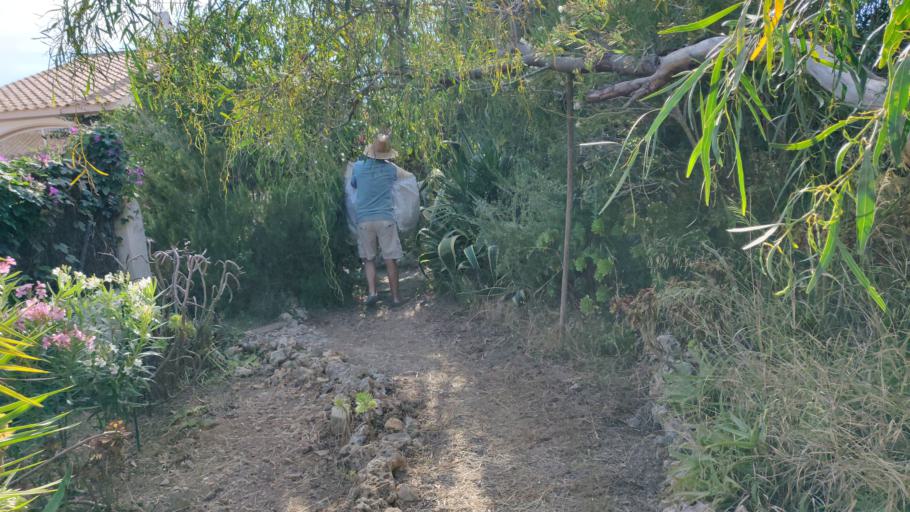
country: ES
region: Balearic Islands
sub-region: Illes Balears
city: Felanitx
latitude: 39.4533
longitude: 3.2609
